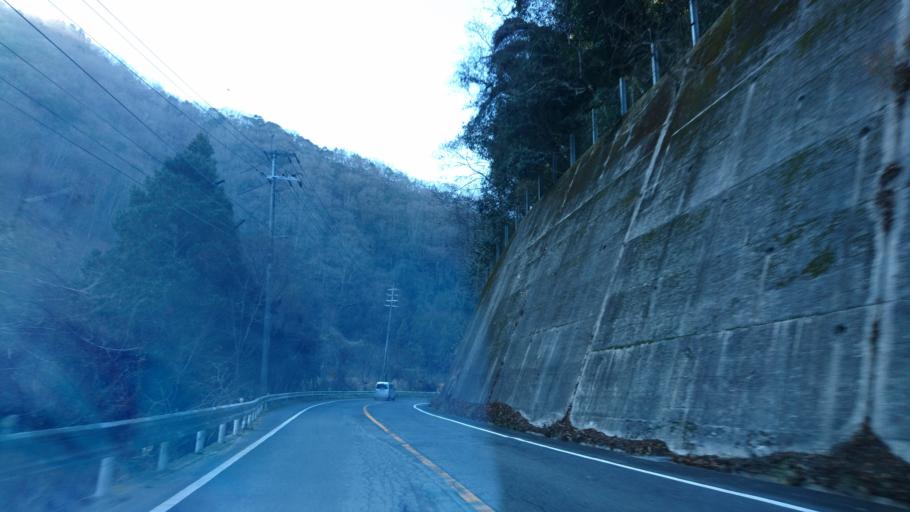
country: JP
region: Okayama
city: Takahashi
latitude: 34.8193
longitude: 133.6520
